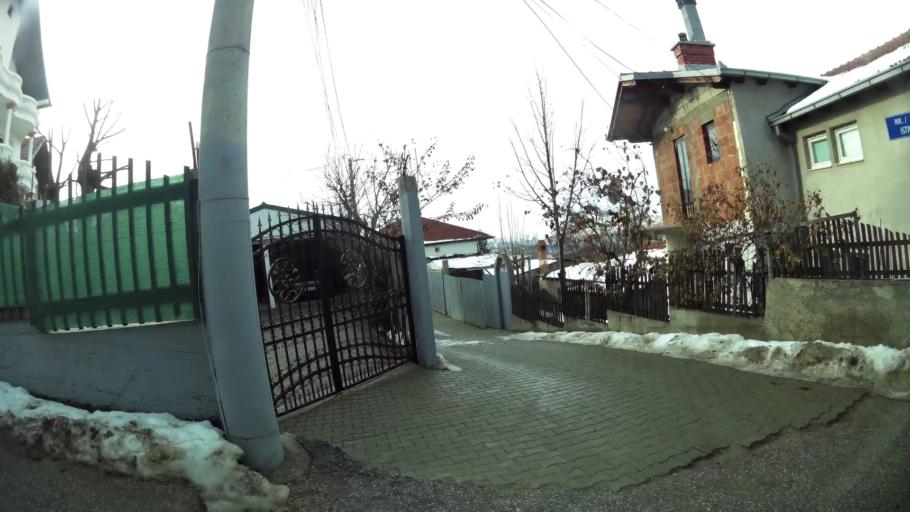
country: XK
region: Pristina
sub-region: Komuna e Prishtines
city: Pristina
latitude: 42.6700
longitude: 21.1806
